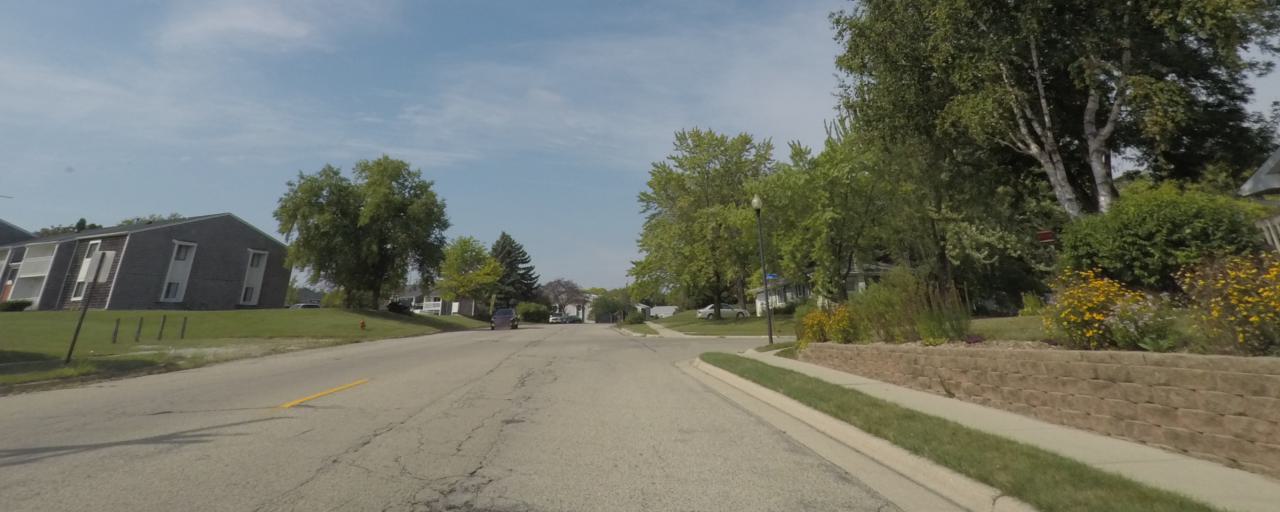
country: US
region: Wisconsin
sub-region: Jefferson County
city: Jefferson
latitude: 42.9906
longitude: -88.8168
